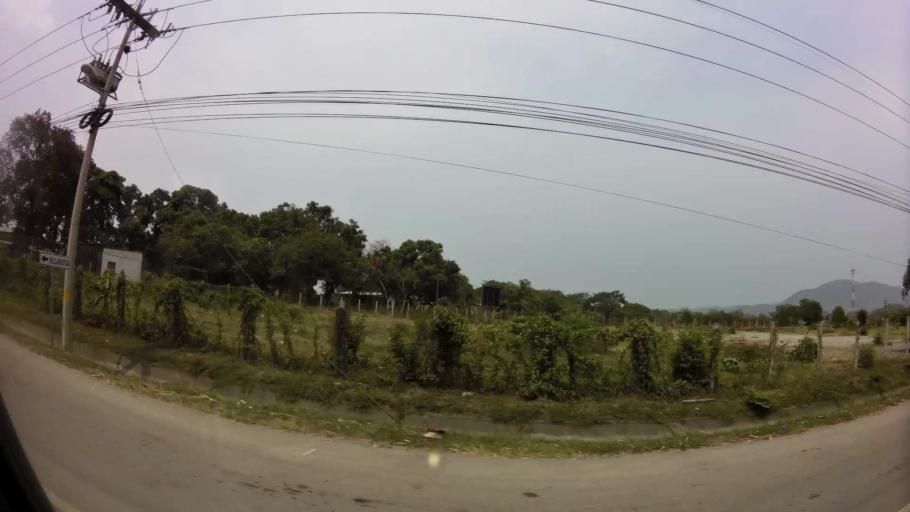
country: HN
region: Cortes
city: Villanueva
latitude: 15.3100
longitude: -87.9881
